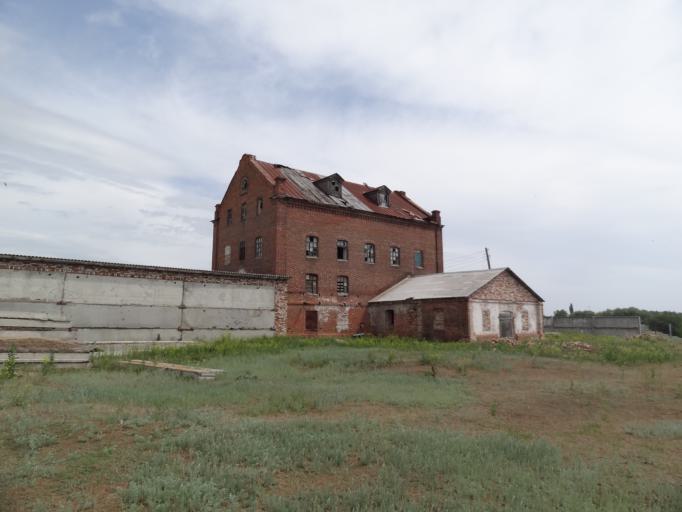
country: RU
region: Saratov
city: Privolzhskiy
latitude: 51.1989
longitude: 45.9079
